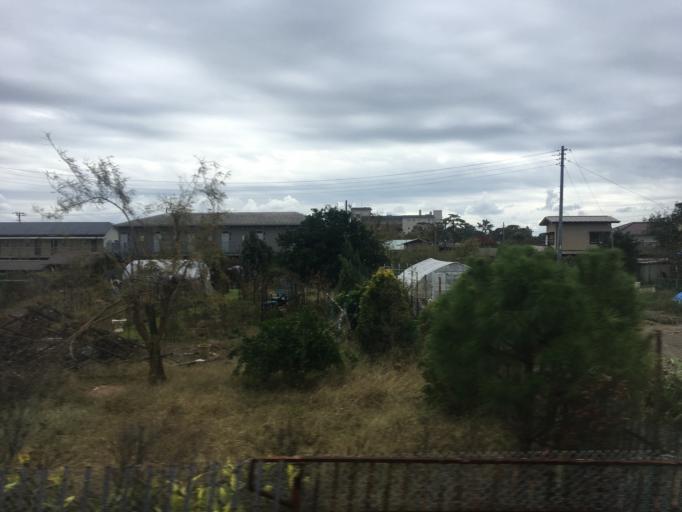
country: JP
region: Chiba
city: Kawaguchi
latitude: 35.1185
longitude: 140.1149
